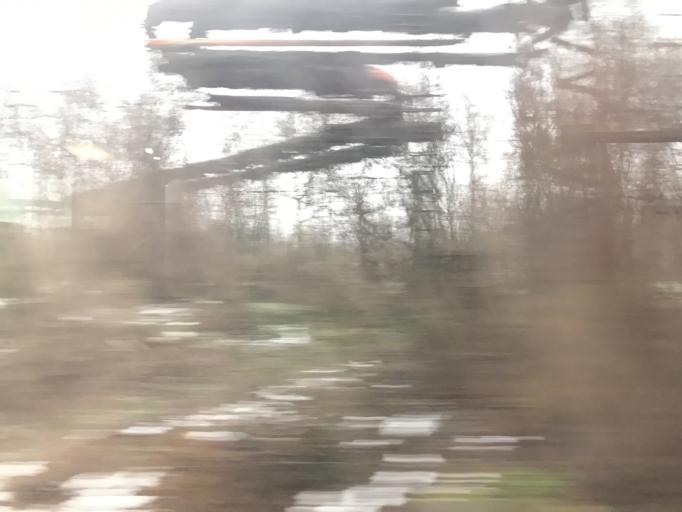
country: HU
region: Gyor-Moson-Sopron
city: Gyor
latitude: 47.6847
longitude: 17.6675
